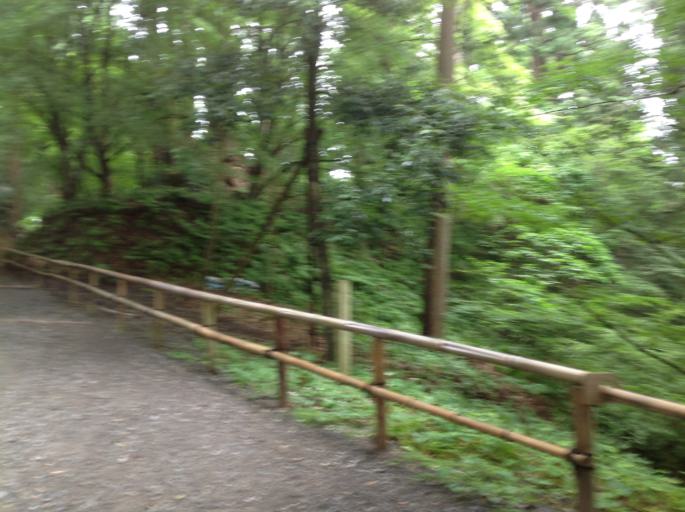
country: JP
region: Iwate
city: Ichinoseki
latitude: 39.0007
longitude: 141.1044
